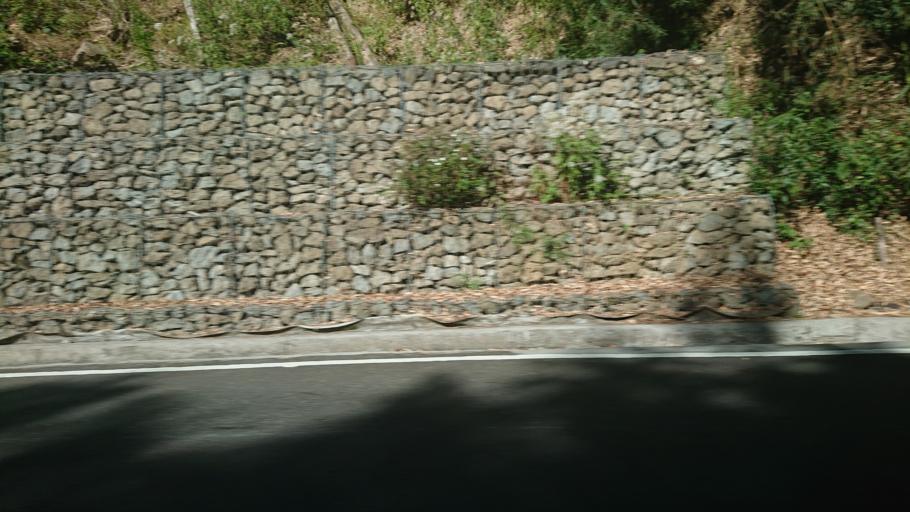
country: TW
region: Taiwan
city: Lugu
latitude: 23.4865
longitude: 120.7459
